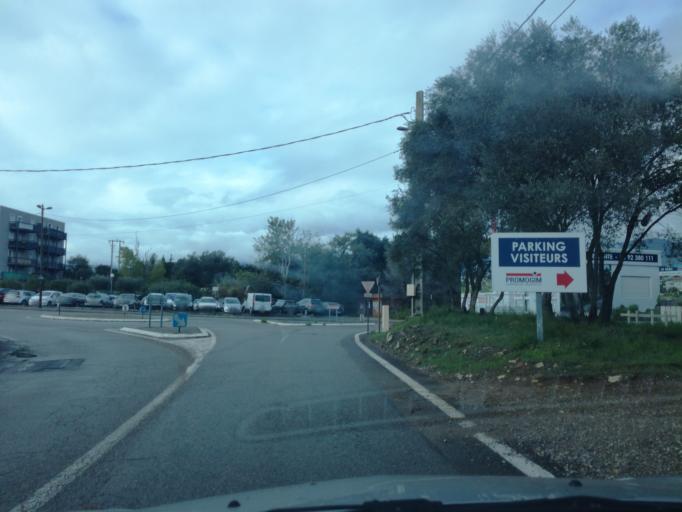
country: FR
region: Provence-Alpes-Cote d'Azur
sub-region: Departement des Alpes-Maritimes
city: Pegomas
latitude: 43.6194
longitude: 6.9332
